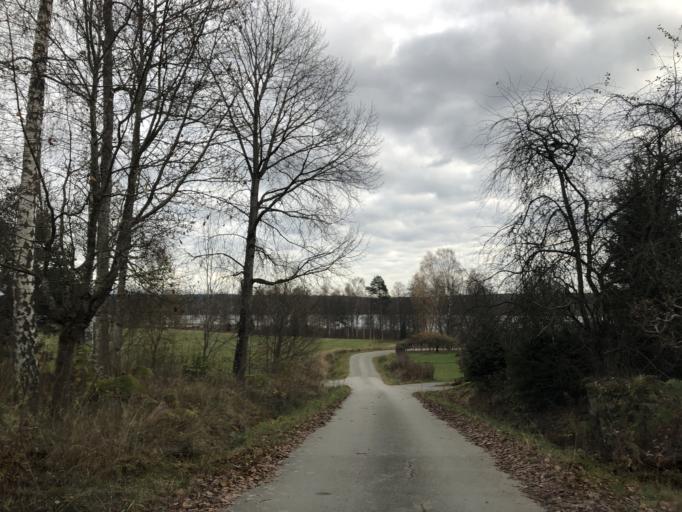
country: SE
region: Vaestra Goetaland
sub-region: Ulricehamns Kommun
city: Ulricehamn
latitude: 57.7359
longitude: 13.3729
